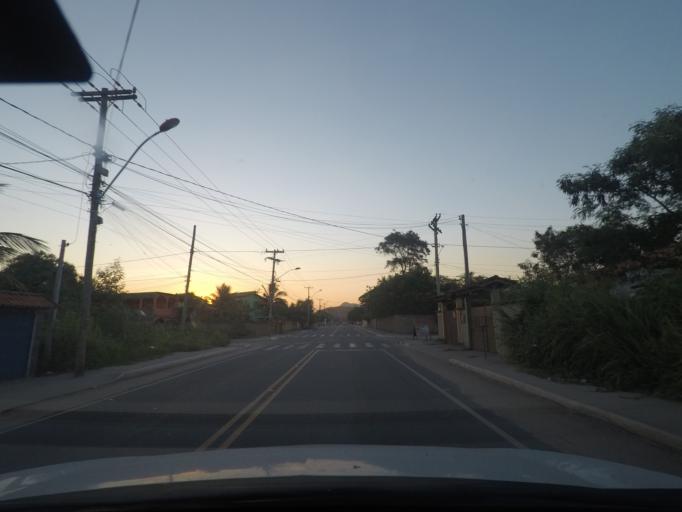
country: BR
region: Rio de Janeiro
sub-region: Marica
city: Marica
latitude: -22.9566
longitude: -42.9583
